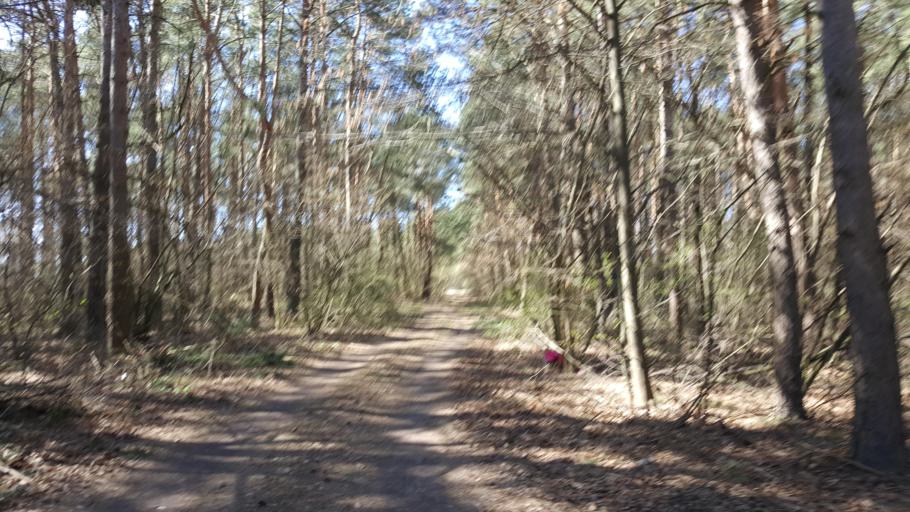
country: BY
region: Brest
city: Zhabinka
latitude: 52.2515
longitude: 23.8848
